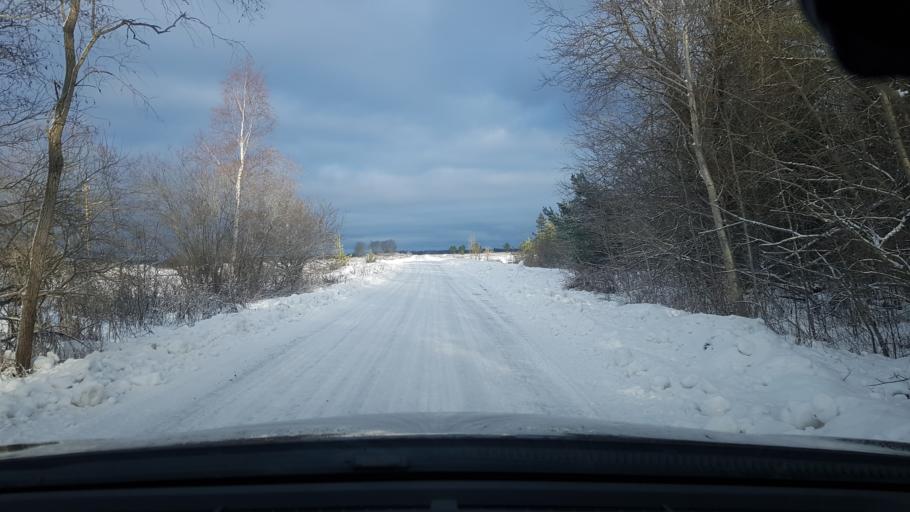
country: EE
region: Harju
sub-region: Keila linn
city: Keila
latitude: 59.3083
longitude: 24.2488
